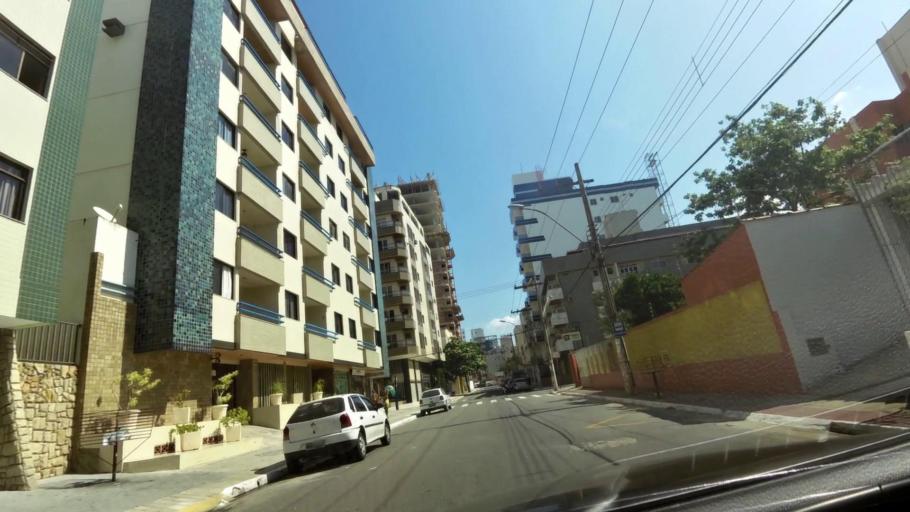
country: BR
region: Espirito Santo
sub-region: Guarapari
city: Guarapari
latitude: -20.6512
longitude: -40.4834
